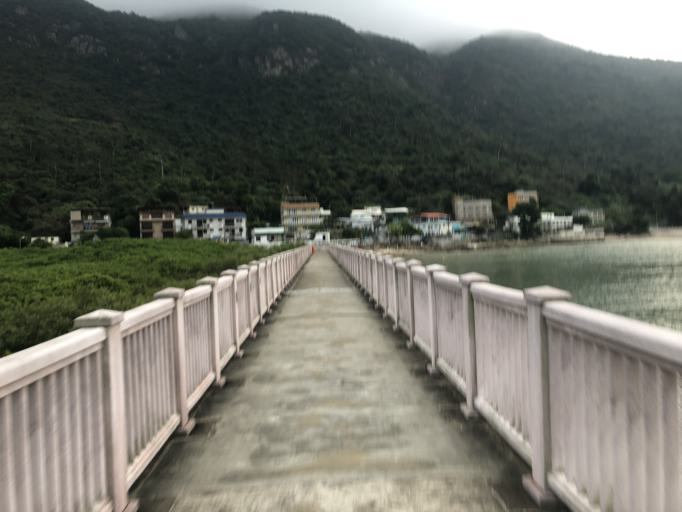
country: HK
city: Tai O
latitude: 22.2479
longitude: 113.8612
